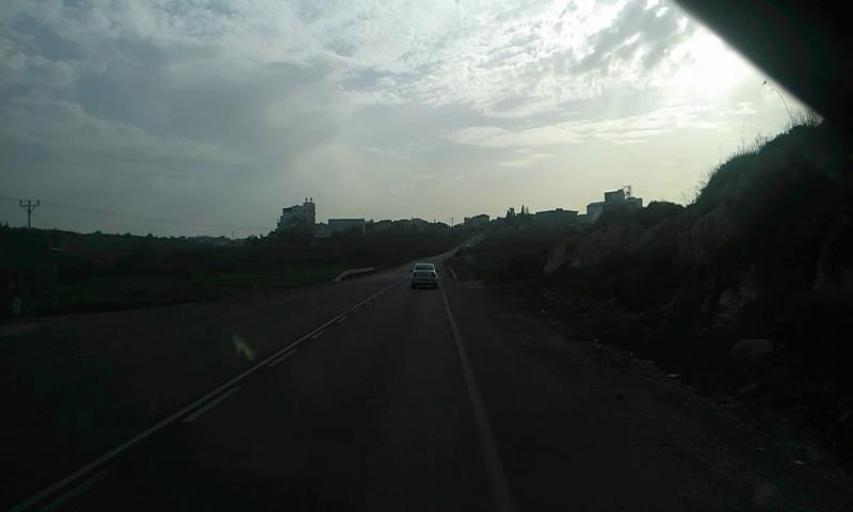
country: PS
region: West Bank
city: Hajjah
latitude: 32.1934
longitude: 35.1406
